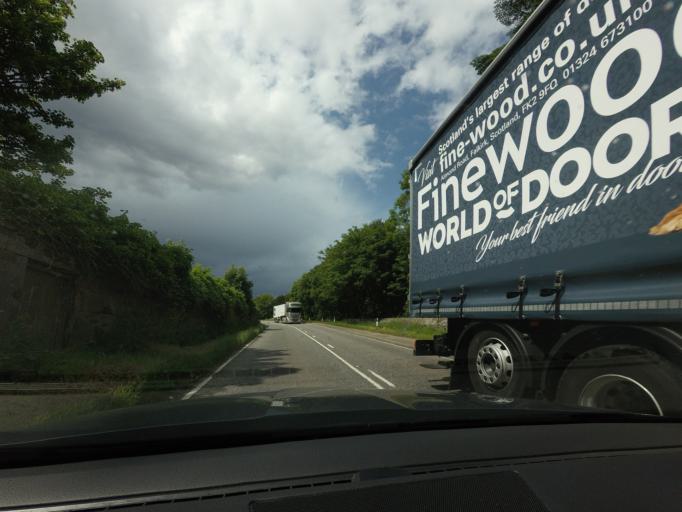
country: GB
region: Scotland
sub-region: Moray
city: Cullen
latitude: 57.6924
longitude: -2.8319
